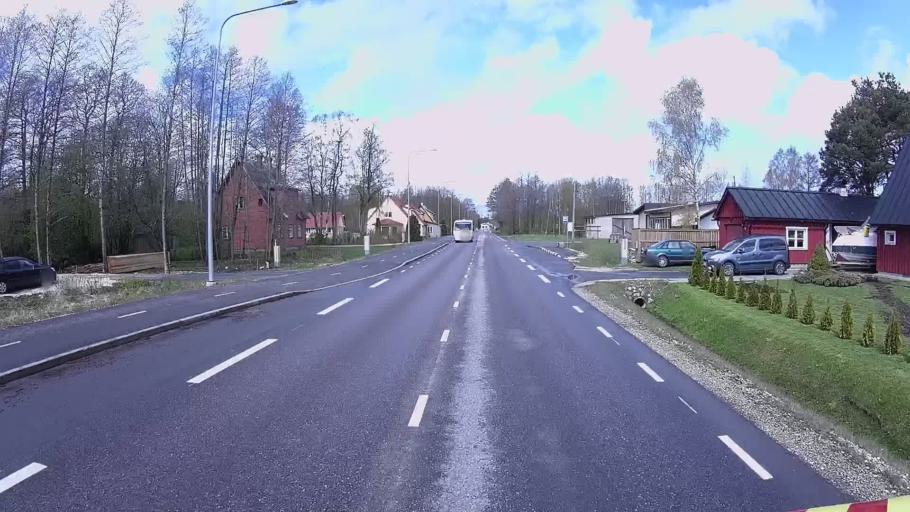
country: EE
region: Hiiumaa
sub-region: Kaerdla linn
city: Kardla
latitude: 58.9869
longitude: 22.7535
